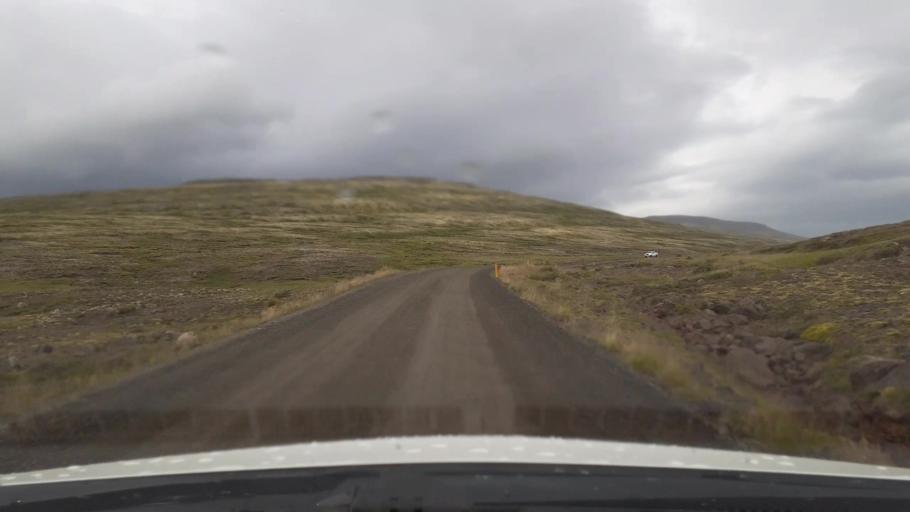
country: IS
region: Capital Region
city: Mosfellsbaer
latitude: 64.4860
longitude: -21.5127
